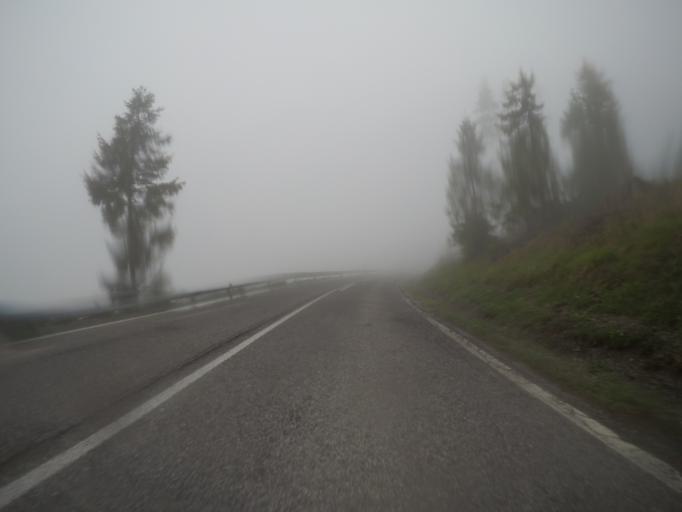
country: SK
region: Presovsky
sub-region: Okres Poprad
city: Strba
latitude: 49.1058
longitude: 20.0677
